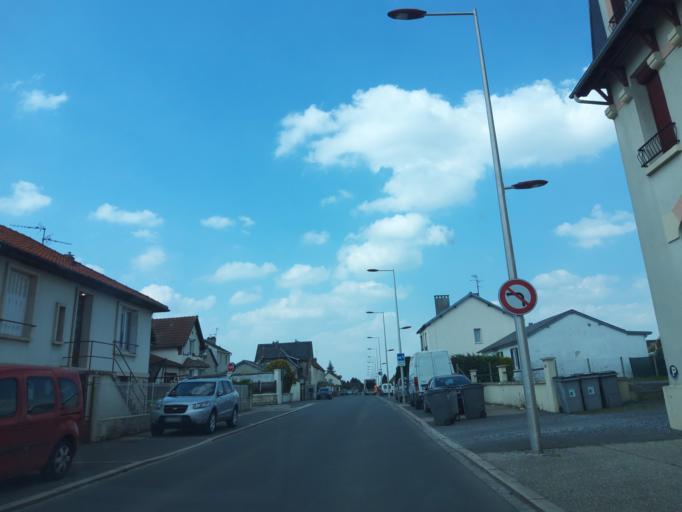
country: FR
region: Picardie
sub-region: Departement de l'Aisne
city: Laon
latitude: 49.5793
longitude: 3.6301
